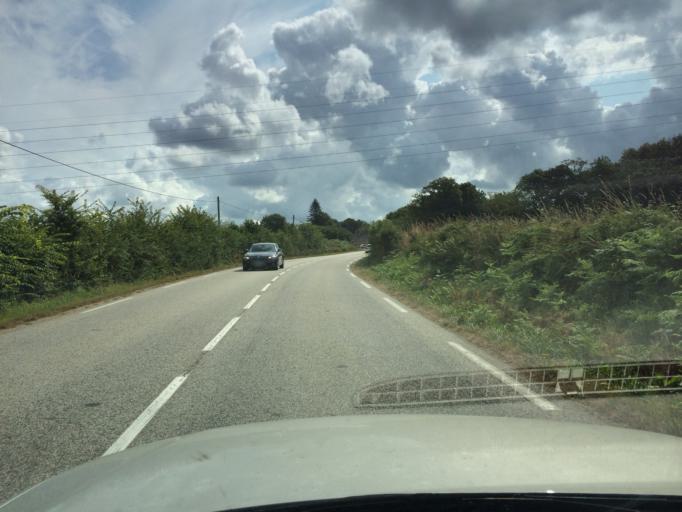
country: FR
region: Lower Normandy
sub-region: Departement de la Manche
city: Tollevast
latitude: 49.5591
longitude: -1.6296
